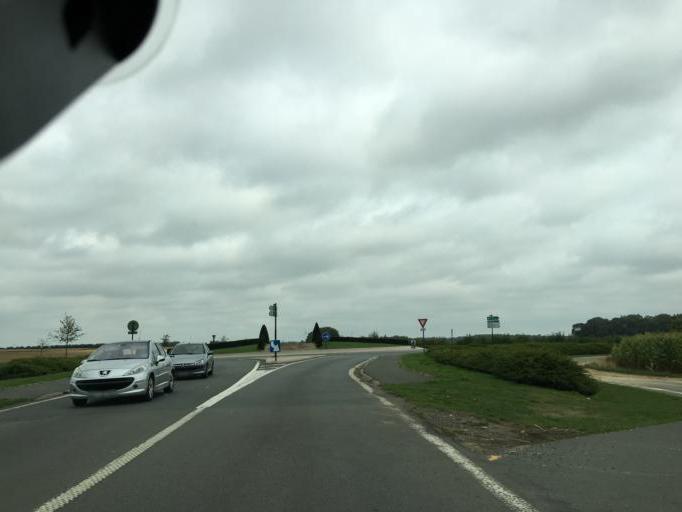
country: FR
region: Nord-Pas-de-Calais
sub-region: Departement du Pas-de-Calais
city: Saint-Pol-sur-Ternoise
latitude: 50.3903
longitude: 2.3521
